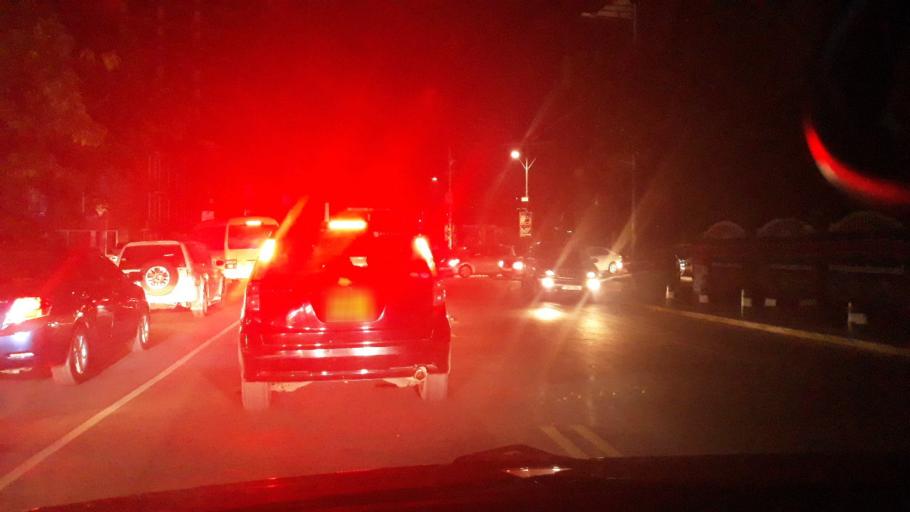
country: KE
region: Nairobi Area
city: Nairobi
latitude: -1.2904
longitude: 36.8216
